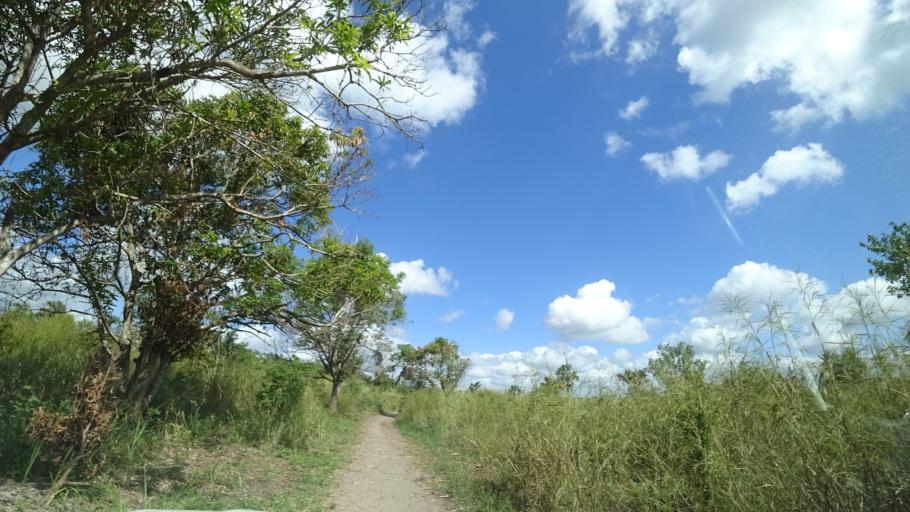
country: MZ
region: Sofala
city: Dondo
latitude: -19.3589
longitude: 34.5783
